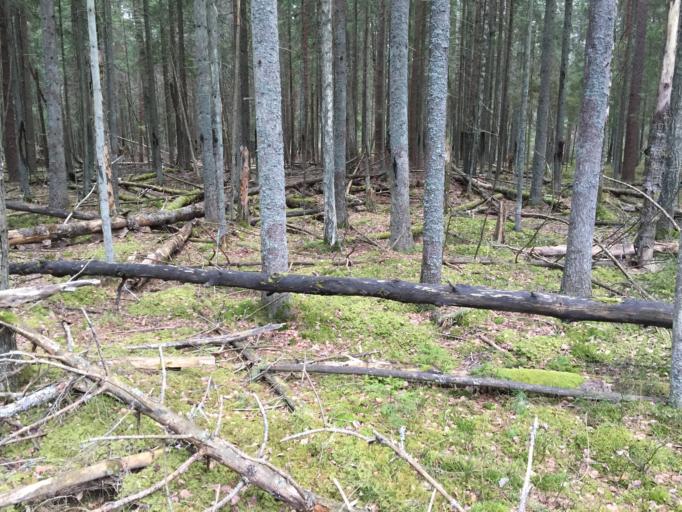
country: LV
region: Garkalne
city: Garkalne
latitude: 56.9574
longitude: 24.4789
